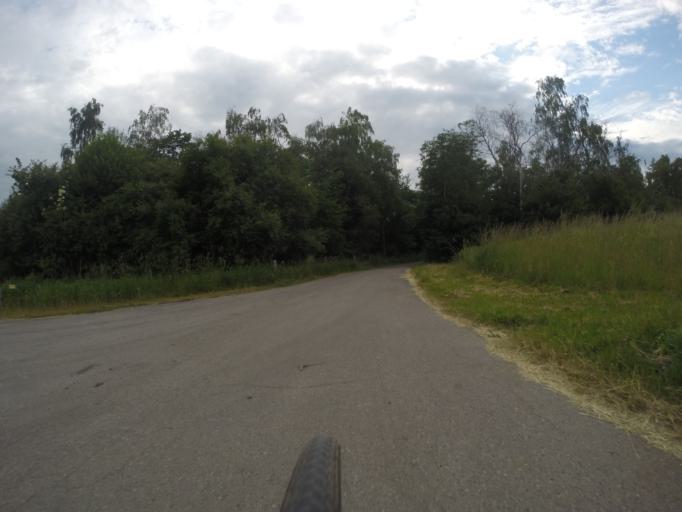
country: DK
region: Capital Region
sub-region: Ballerup Kommune
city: Ballerup
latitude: 55.7007
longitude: 12.3450
